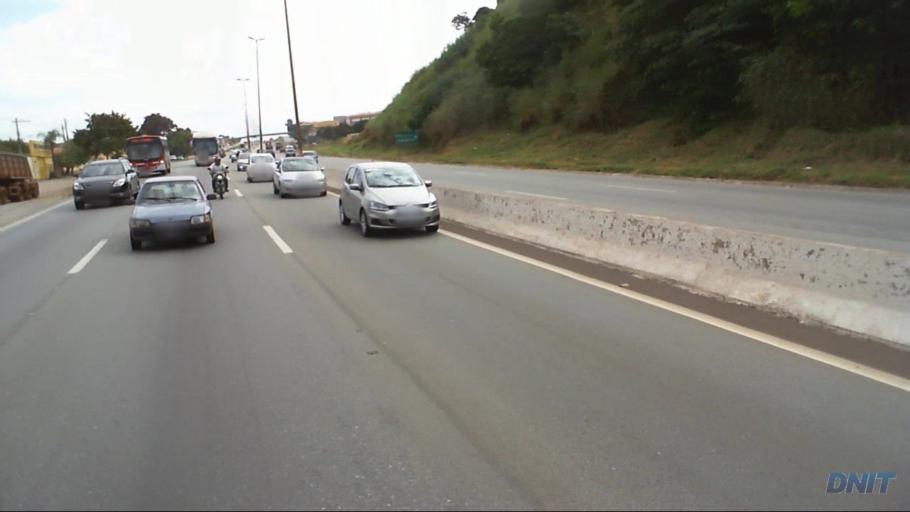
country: BR
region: Minas Gerais
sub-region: Belo Horizonte
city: Belo Horizonte
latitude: -19.8577
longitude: -43.9041
